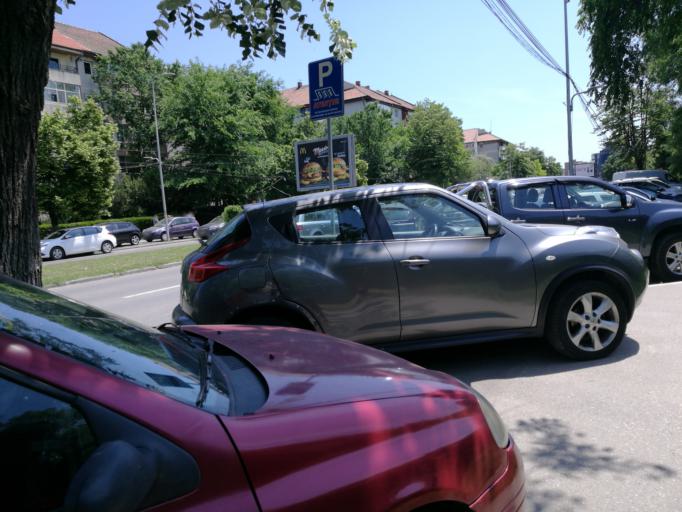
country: RO
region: Constanta
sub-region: Municipiul Constanta
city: Constanta
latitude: 44.2079
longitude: 28.6433
